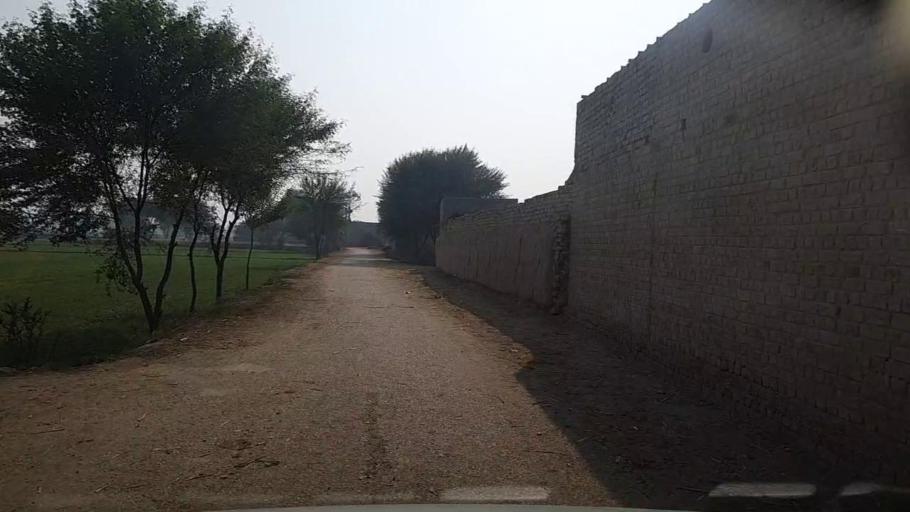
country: PK
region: Sindh
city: Setharja Old
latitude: 27.1250
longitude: 68.5155
